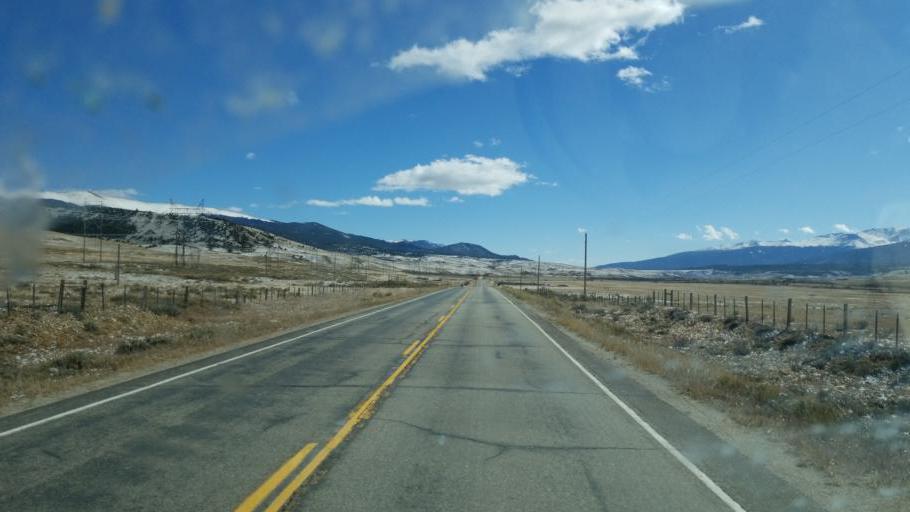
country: US
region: Colorado
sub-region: Lake County
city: Leadville
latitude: 39.1844
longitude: -106.3274
